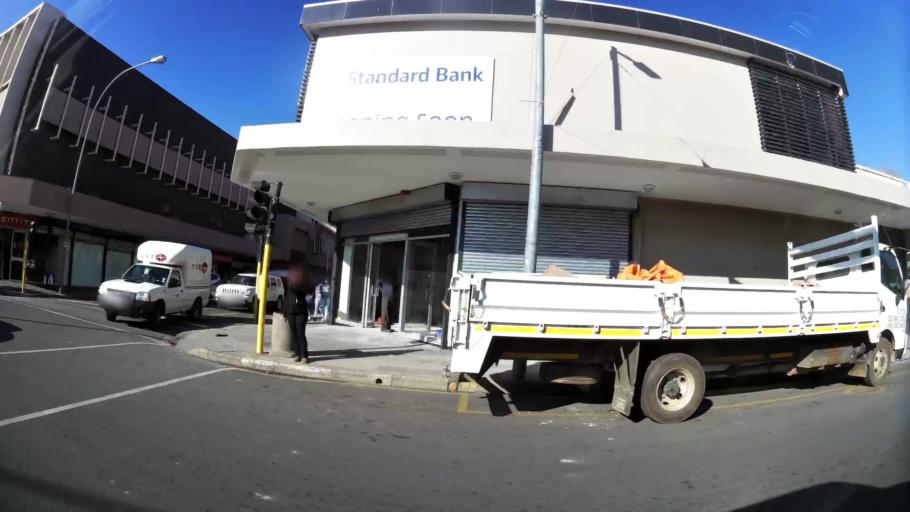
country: ZA
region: Northern Cape
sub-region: Frances Baard District Municipality
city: Kimberley
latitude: -28.7413
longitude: 24.7641
